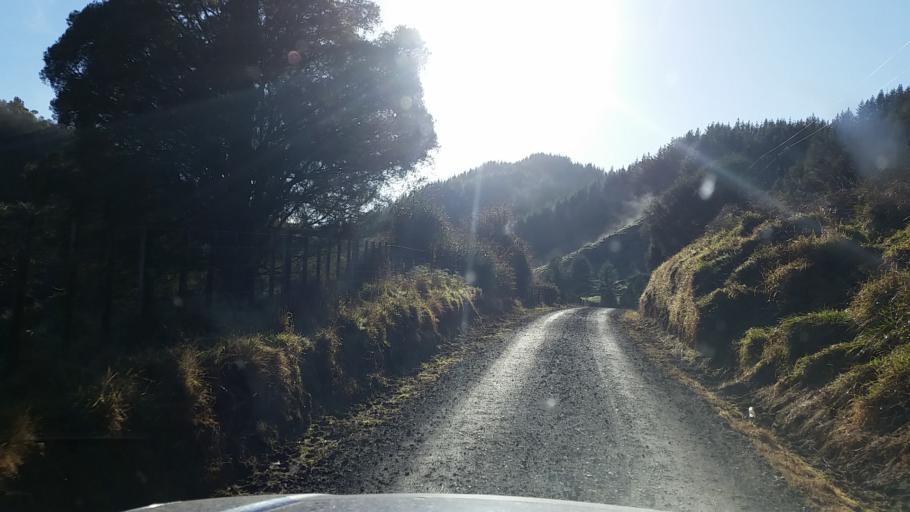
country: NZ
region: Taranaki
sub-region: South Taranaki District
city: Eltham
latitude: -39.3180
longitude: 174.7058
